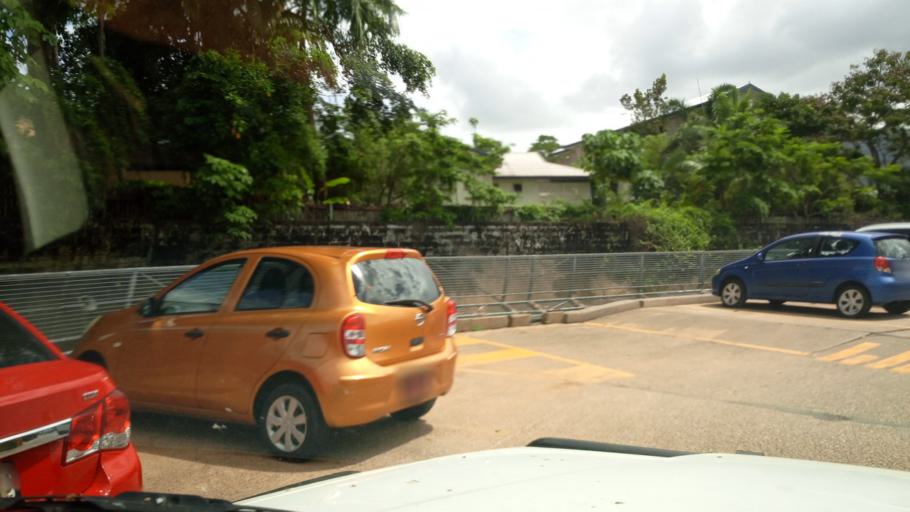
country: AU
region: Queensland
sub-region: Cairns
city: Woree
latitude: -16.9449
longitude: 145.7412
